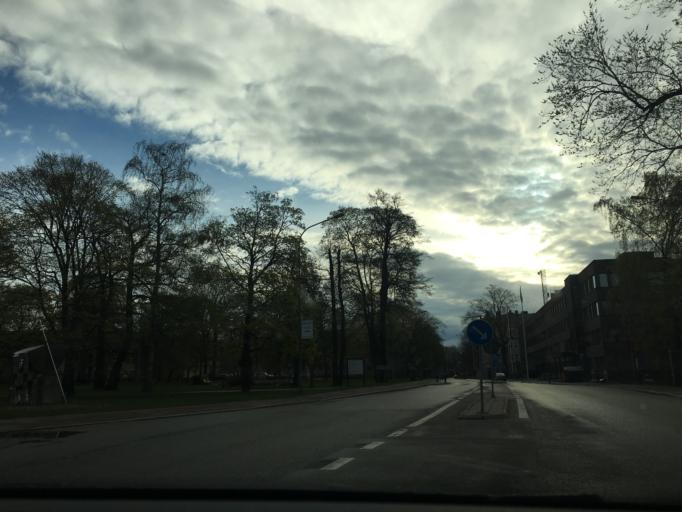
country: SE
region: Vaermland
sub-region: Karlstads Kommun
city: Karlstad
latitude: 59.3817
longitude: 13.4919
